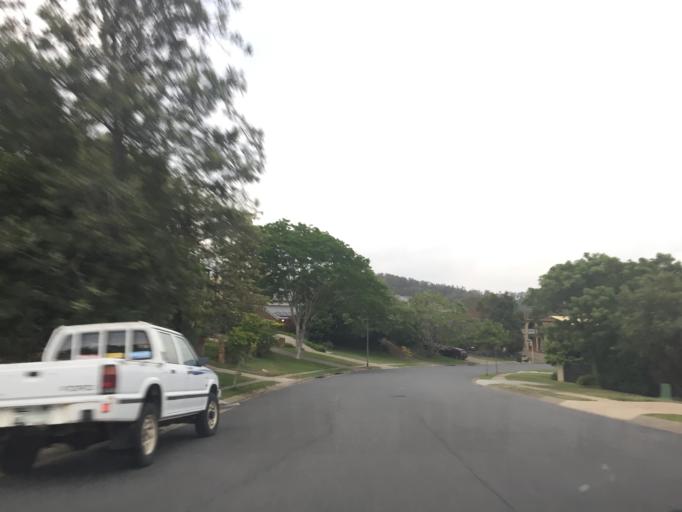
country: AU
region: Queensland
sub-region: Moreton Bay
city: Ferny Hills
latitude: -27.4438
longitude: 152.9350
